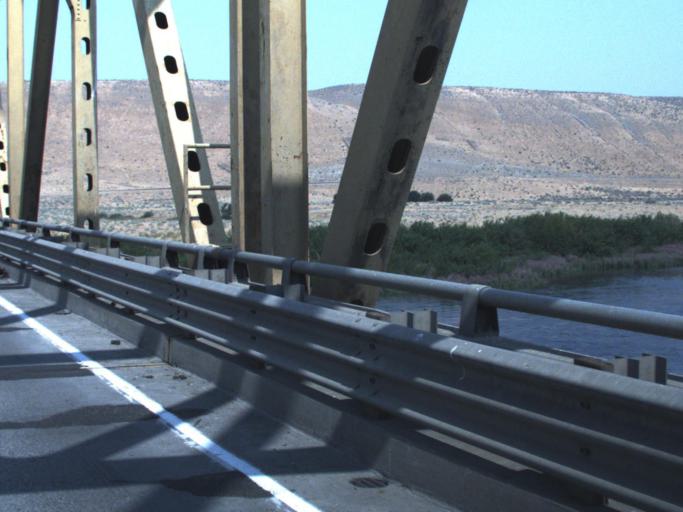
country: US
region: Washington
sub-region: Grant County
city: Desert Aire
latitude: 46.6424
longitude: -119.7327
